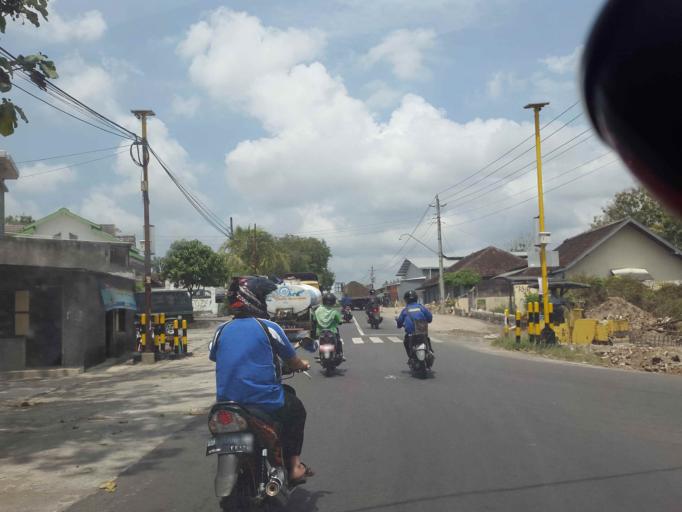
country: ID
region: Daerah Istimewa Yogyakarta
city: Wonosari
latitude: -7.9759
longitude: 110.6001
